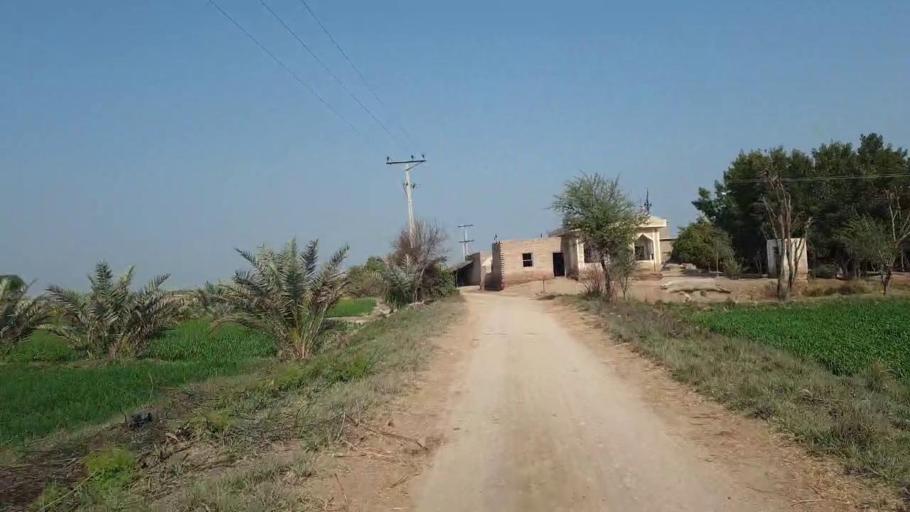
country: PK
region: Sindh
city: Hala
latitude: 25.9201
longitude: 68.4298
